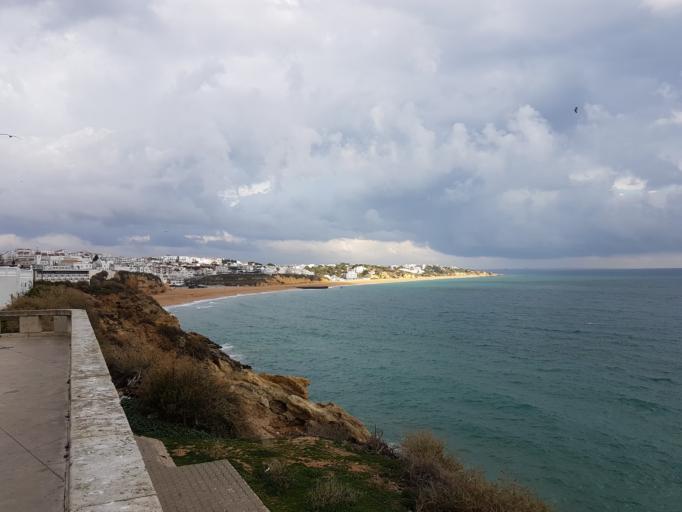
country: PT
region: Faro
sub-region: Albufeira
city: Albufeira
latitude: 37.0841
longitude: -8.2569
